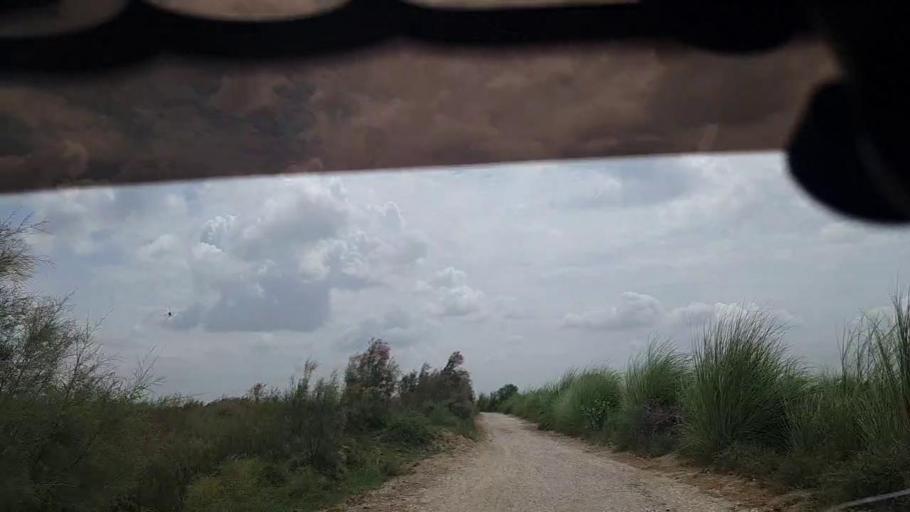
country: PK
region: Sindh
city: Rustam jo Goth
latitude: 28.0512
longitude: 68.9393
